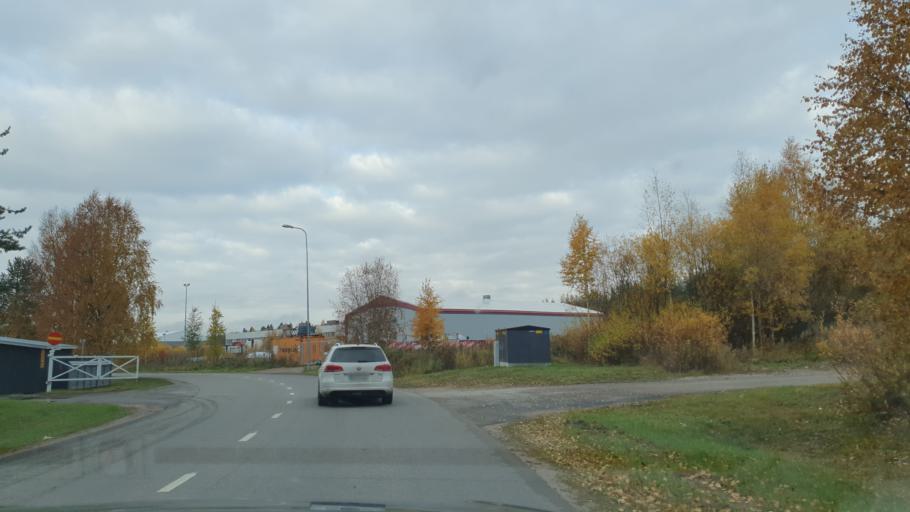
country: FI
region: Lapland
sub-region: Rovaniemi
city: Rovaniemi
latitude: 66.4947
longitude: 25.6721
